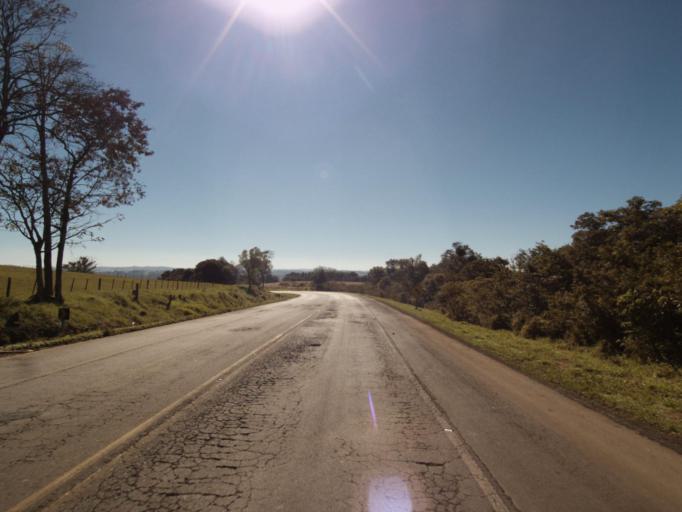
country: BR
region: Santa Catarina
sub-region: Sao Lourenco Do Oeste
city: Sao Lourenco dOeste
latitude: -26.8267
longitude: -53.1807
